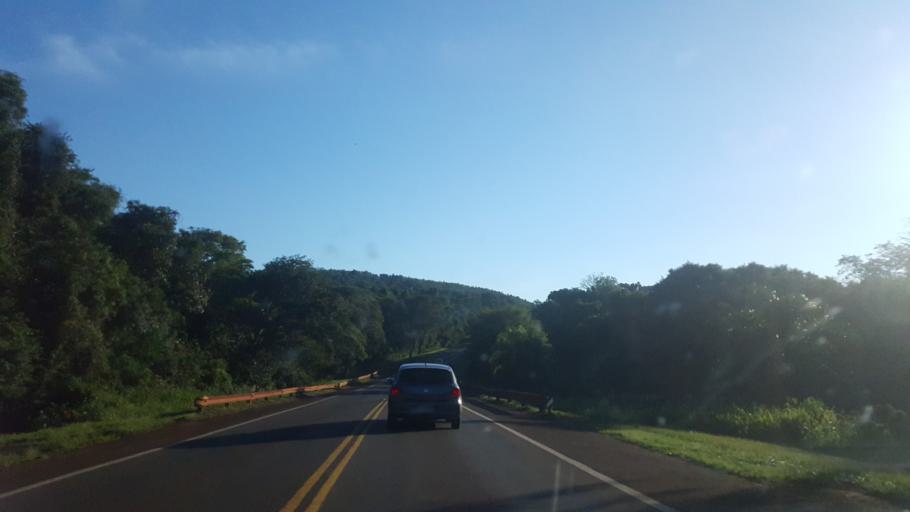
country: AR
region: Misiones
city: El Alcazar
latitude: -26.7181
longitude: -54.8556
